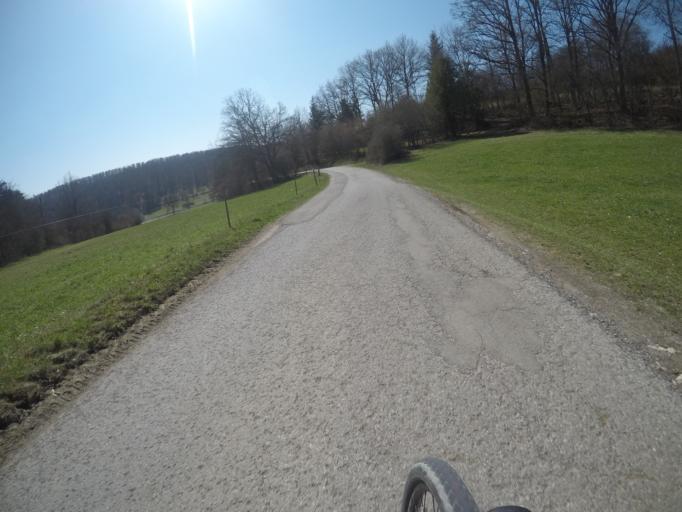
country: DE
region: Baden-Wuerttemberg
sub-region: Karlsruhe Region
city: Gechingen
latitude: 48.7018
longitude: 8.8463
